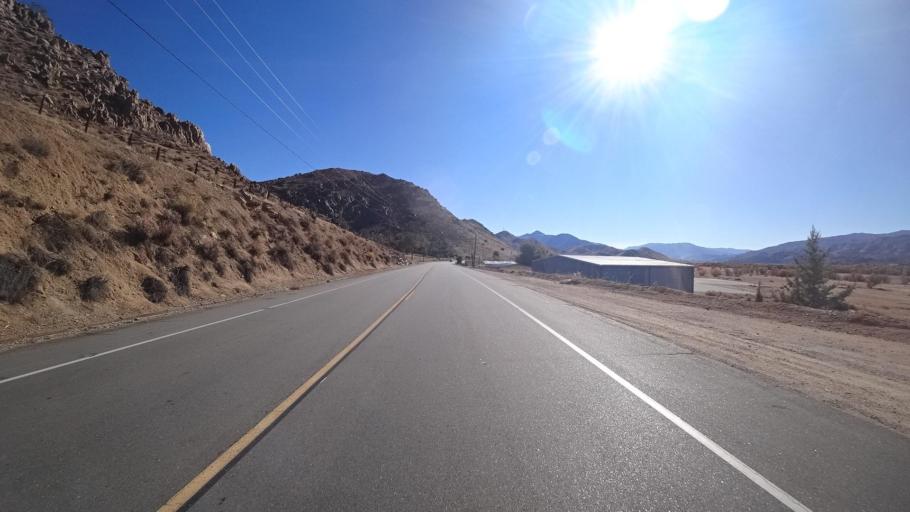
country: US
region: California
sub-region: Kern County
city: Kernville
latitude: 35.7235
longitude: -118.4170
